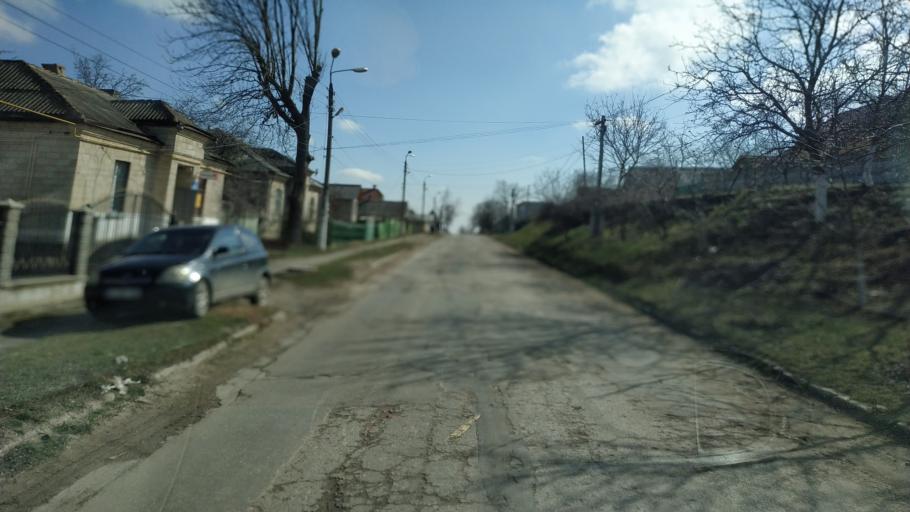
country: MD
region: Hincesti
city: Hincesti
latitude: 46.9699
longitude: 28.5887
